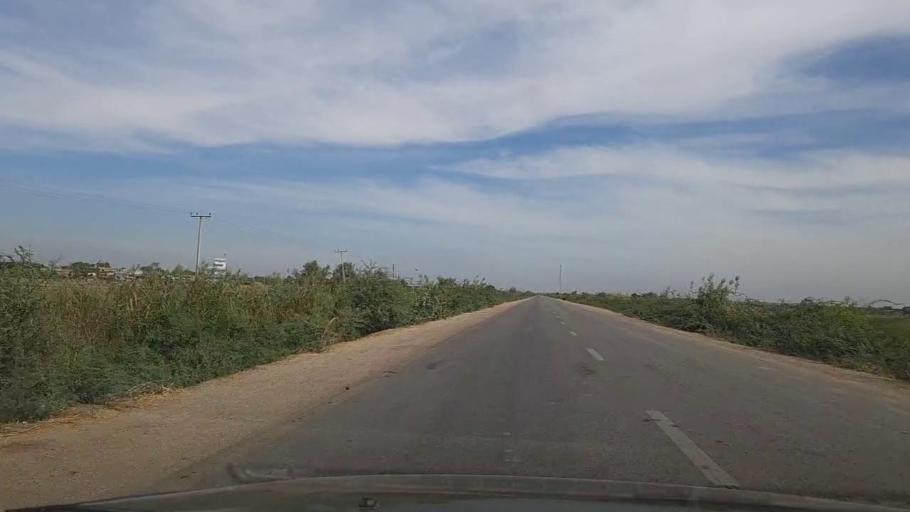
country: PK
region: Sindh
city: Thatta
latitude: 24.8042
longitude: 67.9690
